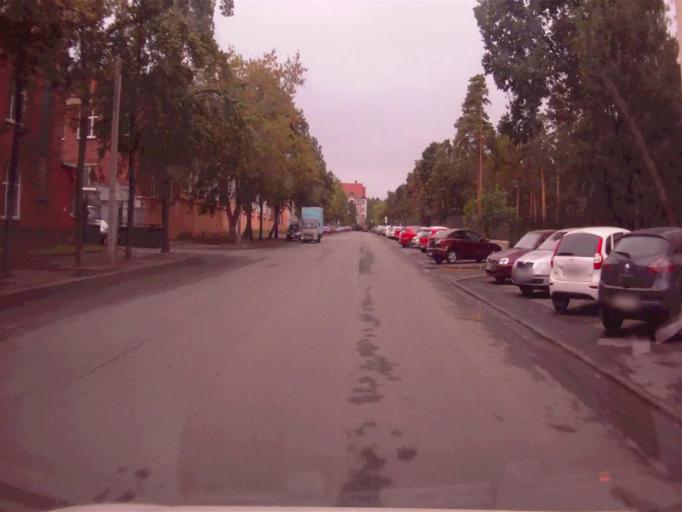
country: RU
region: Chelyabinsk
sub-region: Gorod Chelyabinsk
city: Chelyabinsk
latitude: 55.1616
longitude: 61.3682
